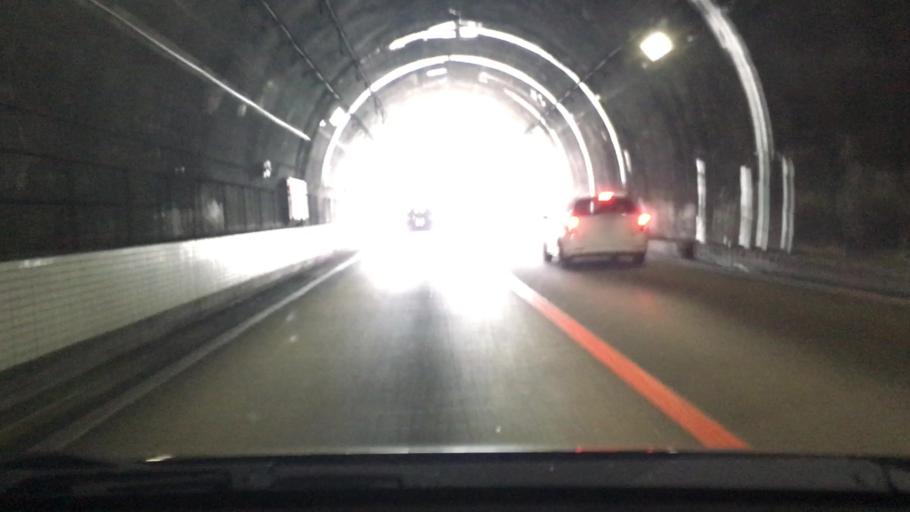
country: JP
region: Yamaguchi
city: Otake
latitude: 34.1847
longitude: 132.1711
